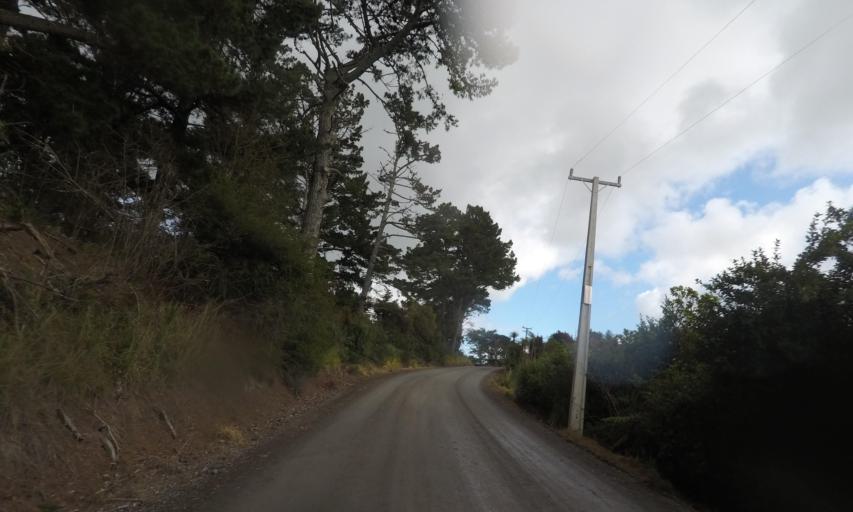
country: NZ
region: Auckland
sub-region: Auckland
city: Wellsford
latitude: -36.1731
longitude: 174.5988
